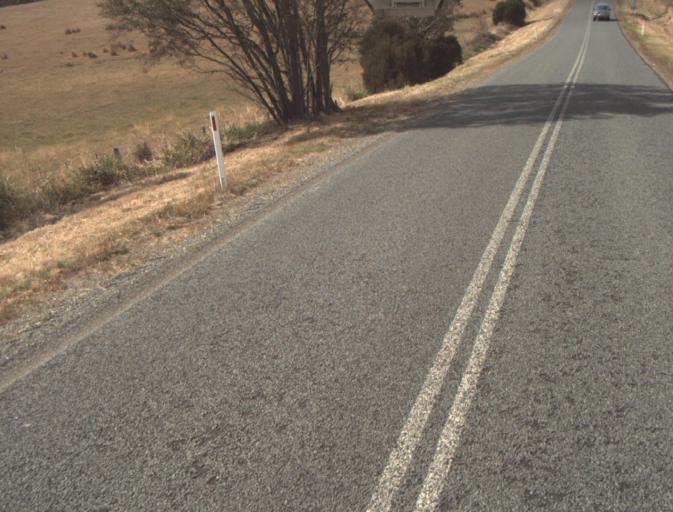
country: AU
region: Tasmania
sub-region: Launceston
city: Mayfield
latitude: -41.2083
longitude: 147.1189
